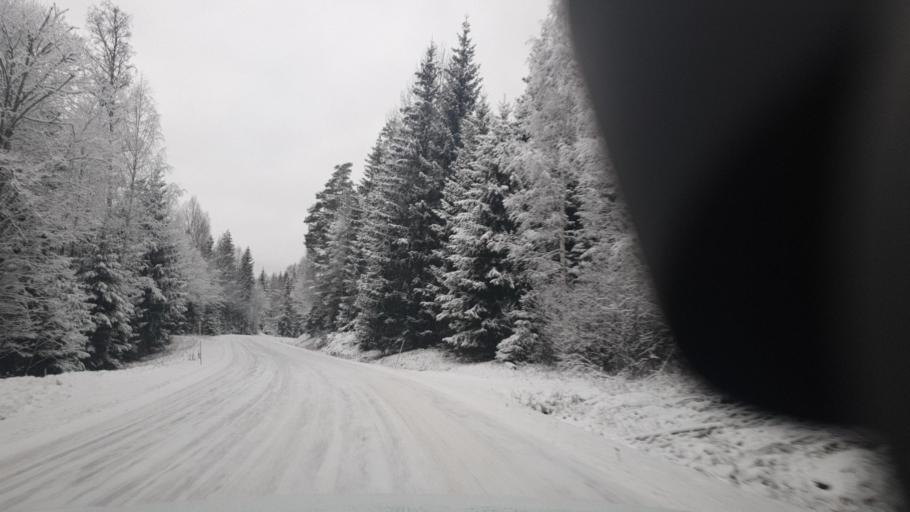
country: NO
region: Hedmark
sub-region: Eidskog
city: Skotterud
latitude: 59.8113
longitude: 12.0289
